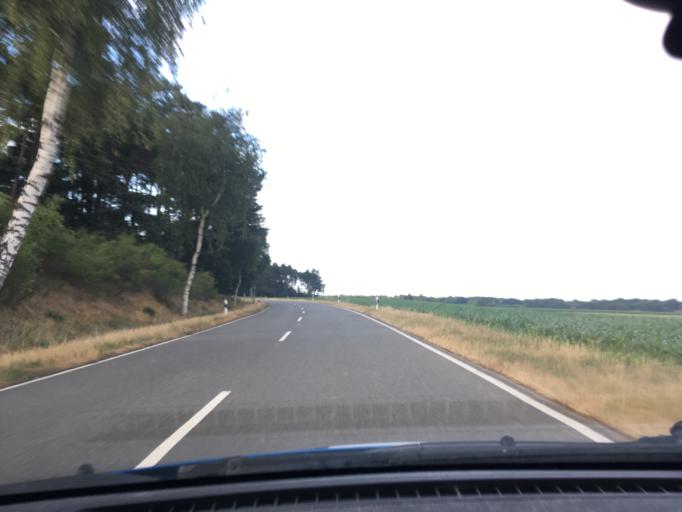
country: DE
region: Lower Saxony
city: Bispingen
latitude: 53.1148
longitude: 9.9407
